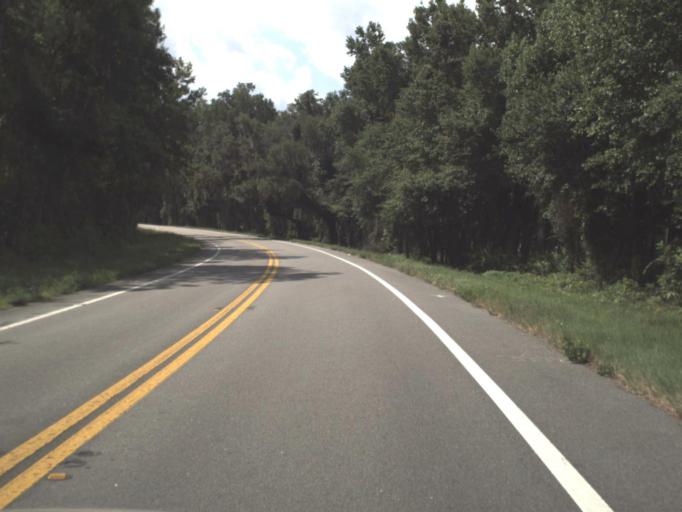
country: US
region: Florida
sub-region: Clay County
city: Green Cove Springs
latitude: 30.0232
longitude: -81.6429
